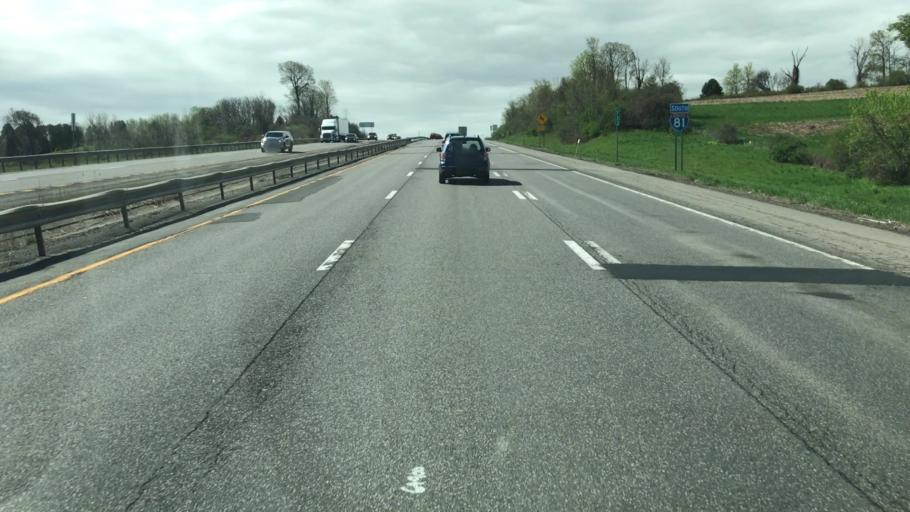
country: US
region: New York
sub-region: Onondaga County
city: Nedrow
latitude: 42.8863
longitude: -76.1098
